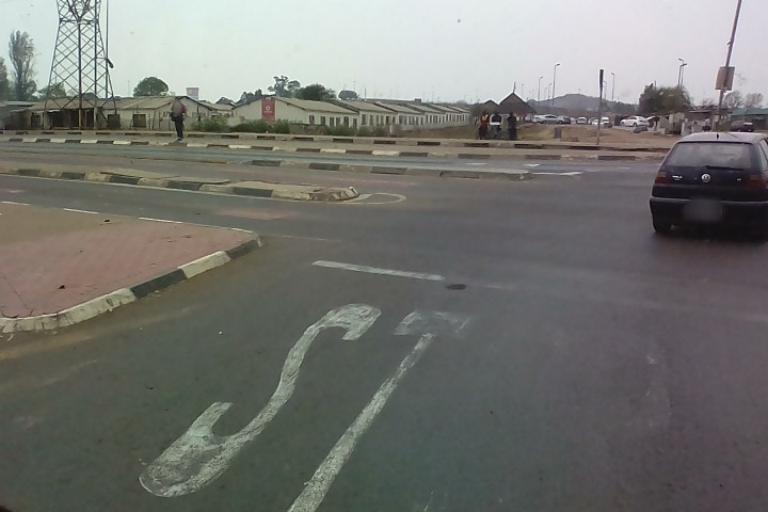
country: ZA
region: Gauteng
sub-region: City of Johannesburg Metropolitan Municipality
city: Soweto
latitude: -26.2526
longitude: 27.8985
